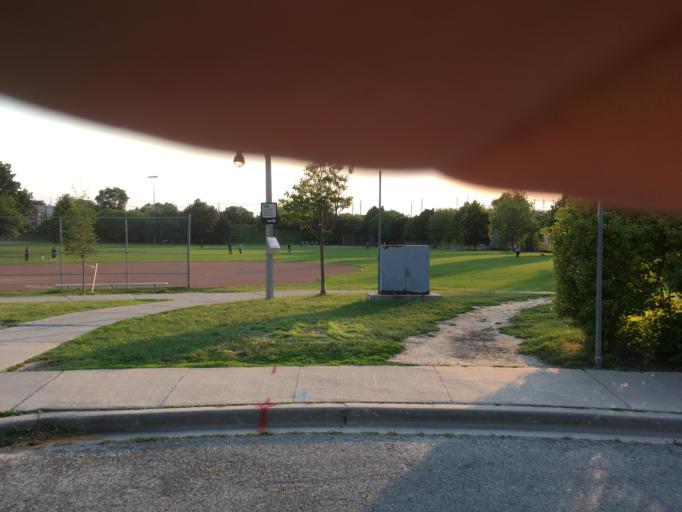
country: CA
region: Ontario
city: Scarborough
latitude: 43.6861
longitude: -79.2981
